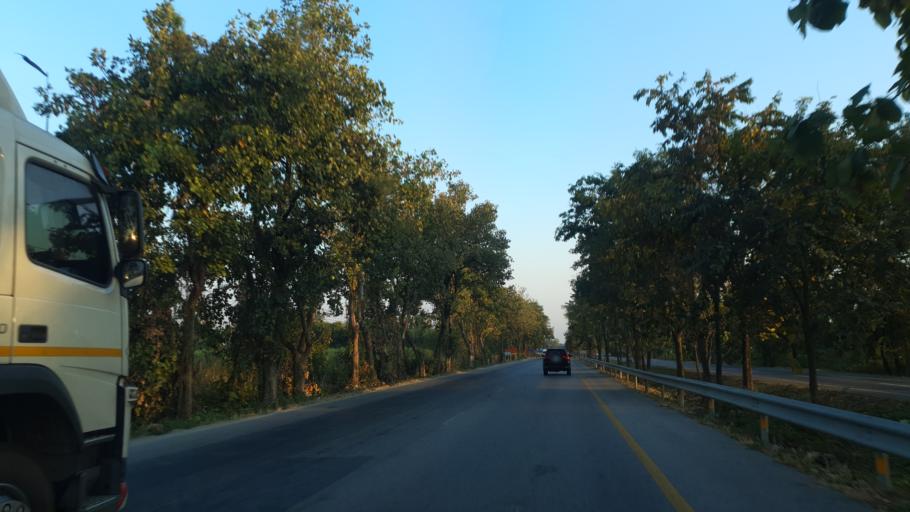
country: TH
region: Nakhon Sawan
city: Banphot Phisai
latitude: 15.9220
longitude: 99.8780
